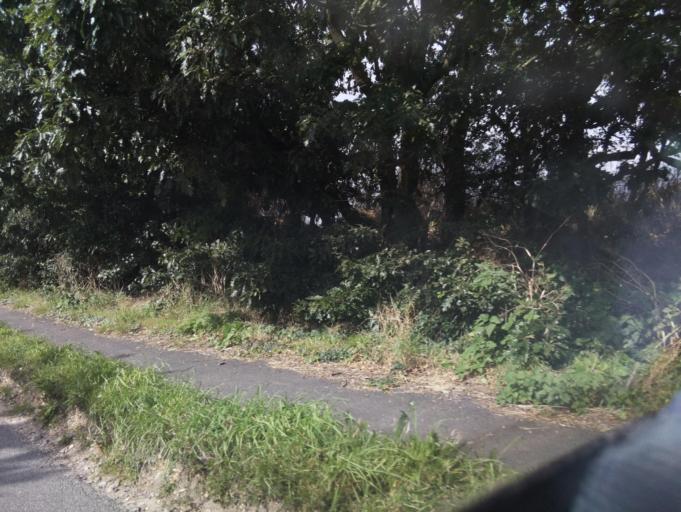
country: GB
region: England
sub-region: Hampshire
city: Milford on Sea
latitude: 50.7310
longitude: -1.6208
